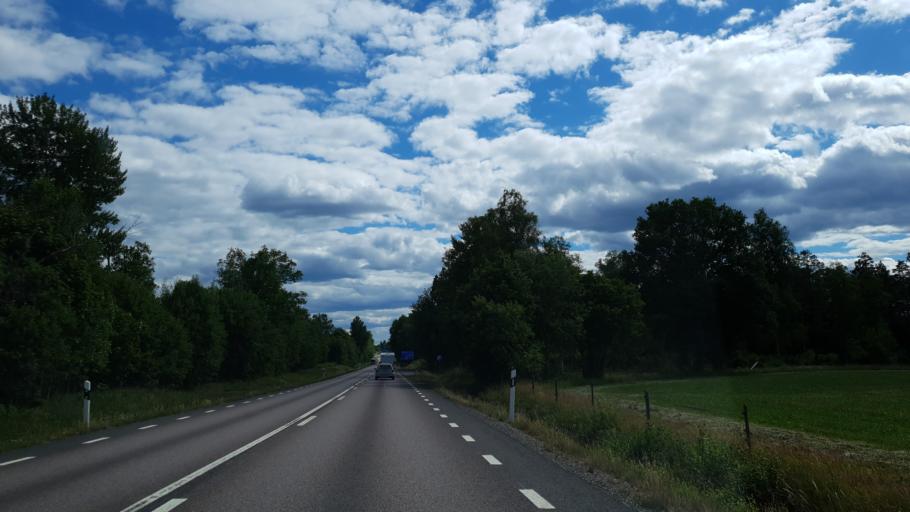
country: SE
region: Kronoberg
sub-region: Lessebo Kommun
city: Lessebo
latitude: 56.8565
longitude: 15.3882
